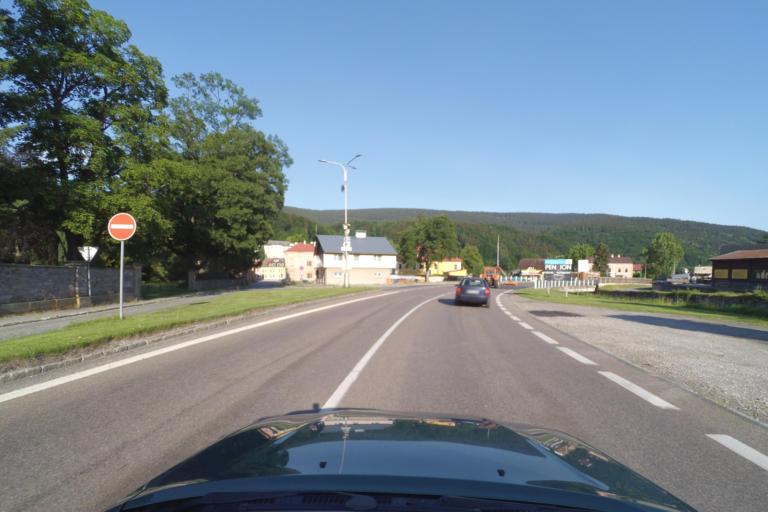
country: CZ
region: Kralovehradecky
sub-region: Okres Trutnov
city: Svoboda nad Upou
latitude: 50.6616
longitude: 15.8181
